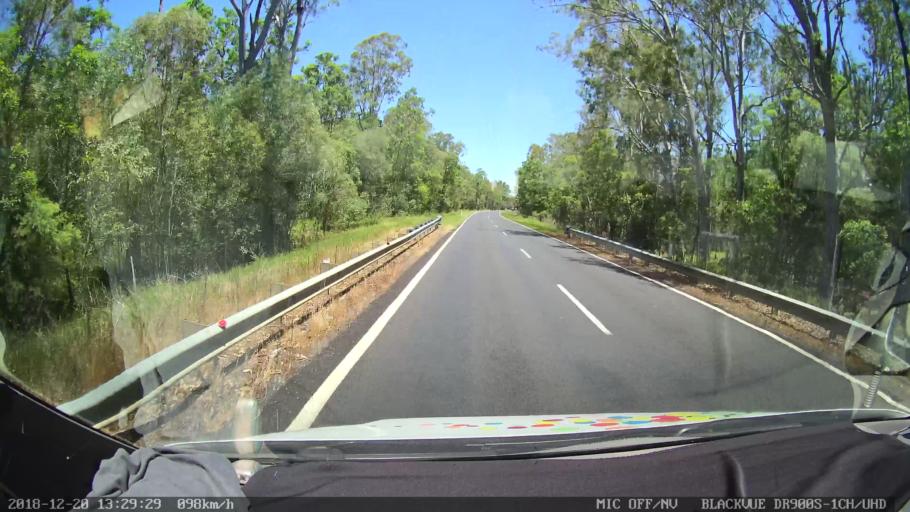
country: AU
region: New South Wales
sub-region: Clarence Valley
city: Gordon
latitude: -29.1896
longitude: 152.9898
